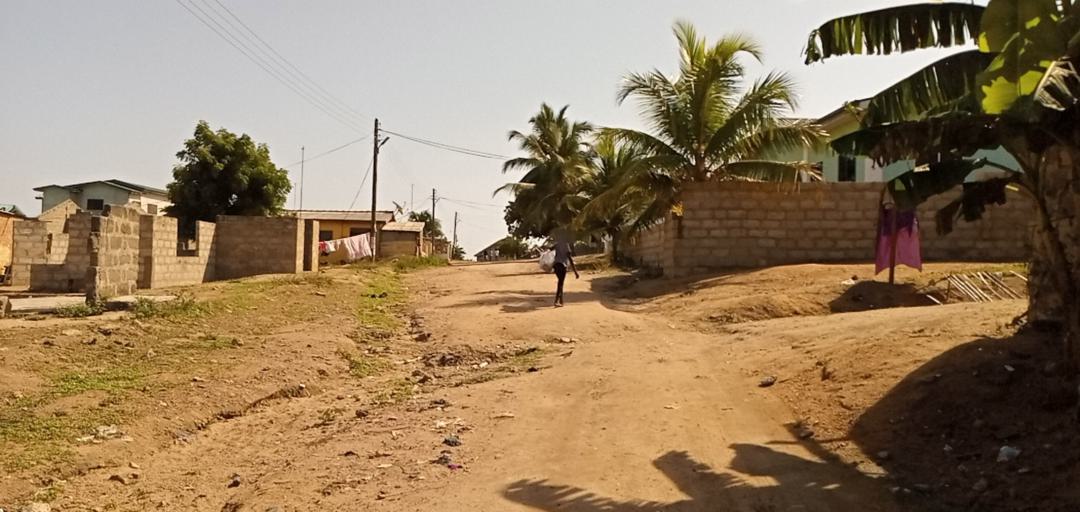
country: GH
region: Central
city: Winneba
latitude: 5.3557
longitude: -0.6211
